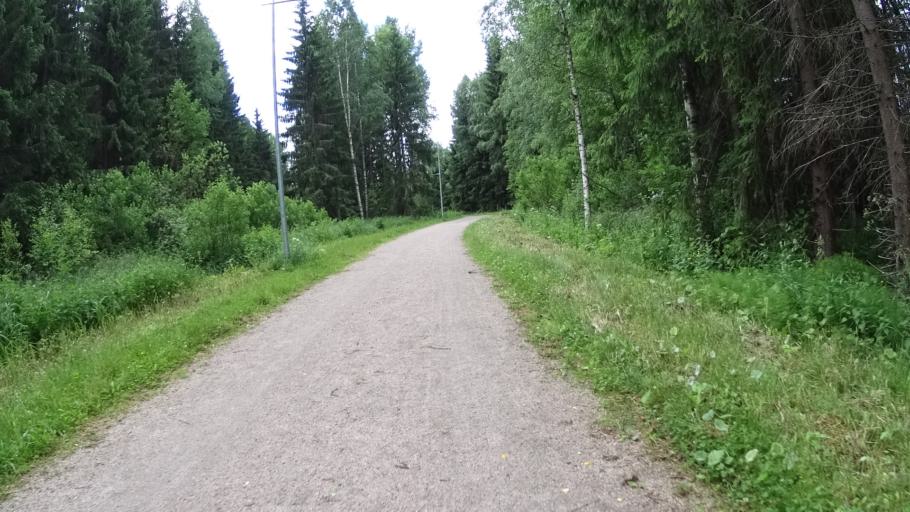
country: FI
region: Uusimaa
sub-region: Helsinki
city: Kilo
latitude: 60.2436
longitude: 24.7973
